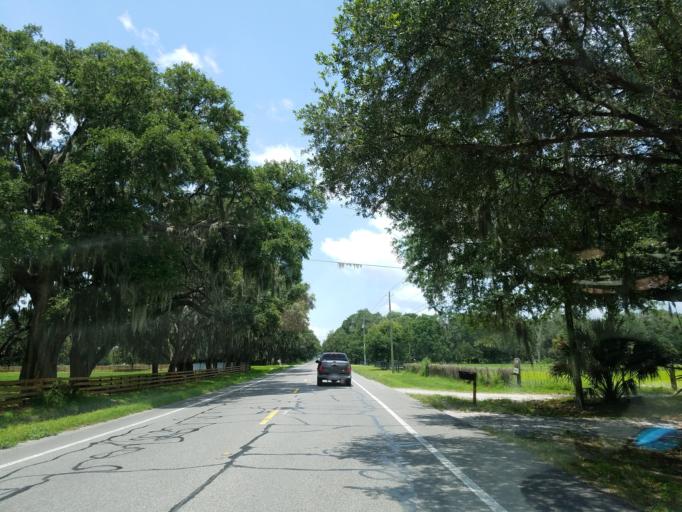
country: US
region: Florida
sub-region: Hillsborough County
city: Fish Hawk
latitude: 27.8506
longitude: -82.1367
